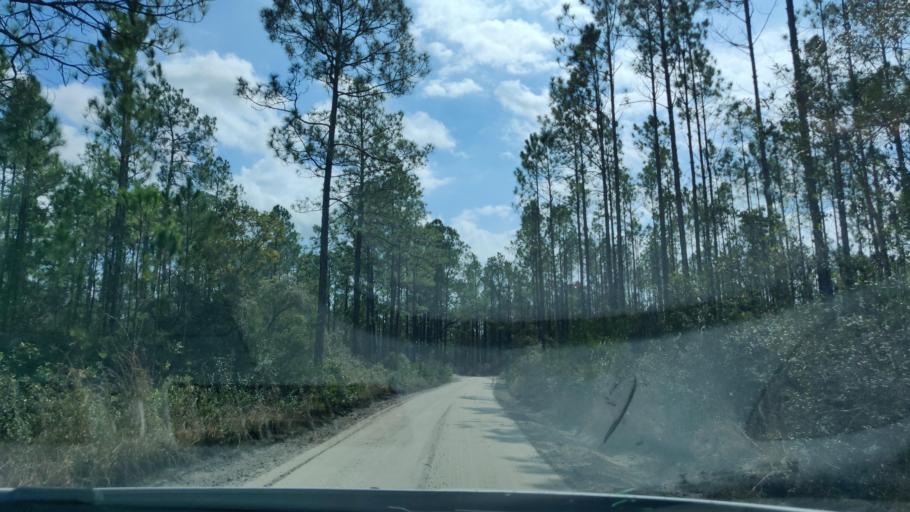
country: US
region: Florida
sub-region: Clay County
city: Middleburg
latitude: 30.1673
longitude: -81.9501
